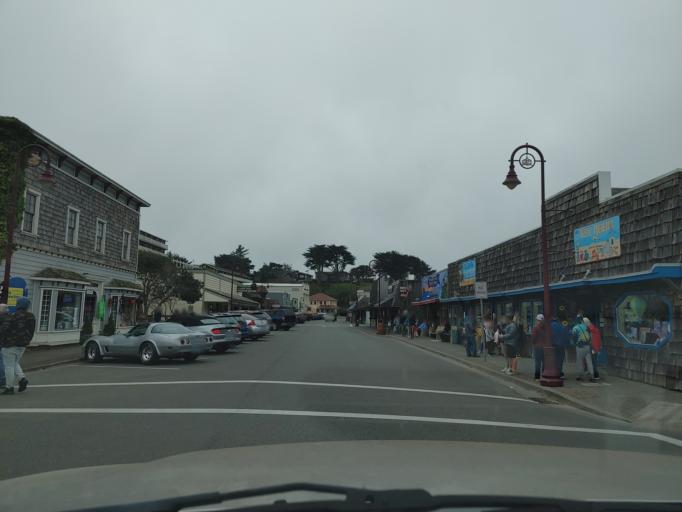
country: US
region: Oregon
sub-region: Coos County
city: Bandon
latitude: 43.1191
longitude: -124.4125
